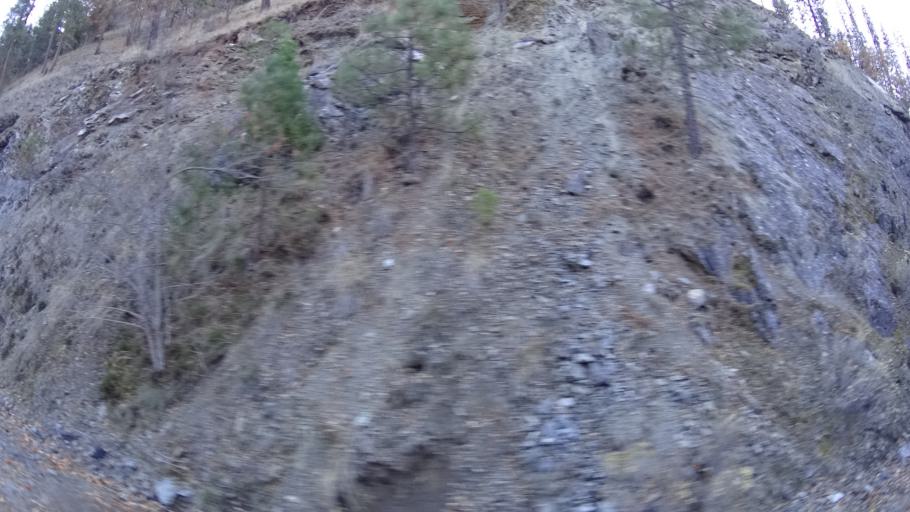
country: US
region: California
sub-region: Siskiyou County
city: Yreka
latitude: 41.8339
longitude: -122.9452
